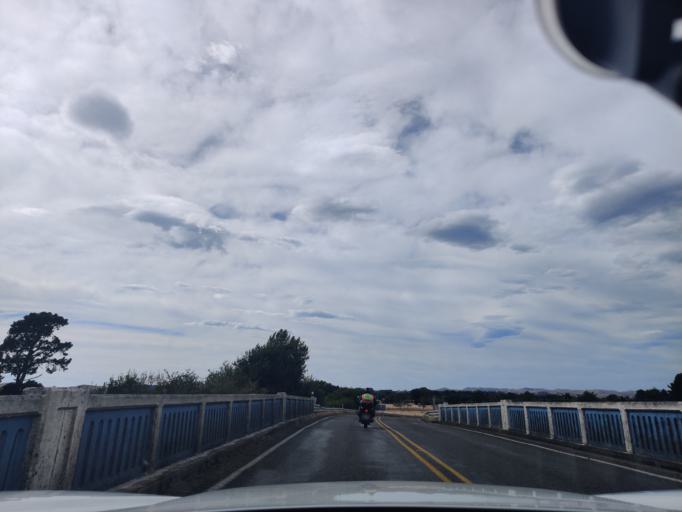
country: NZ
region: Wellington
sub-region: Masterton District
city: Masterton
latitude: -40.8946
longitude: 175.6620
